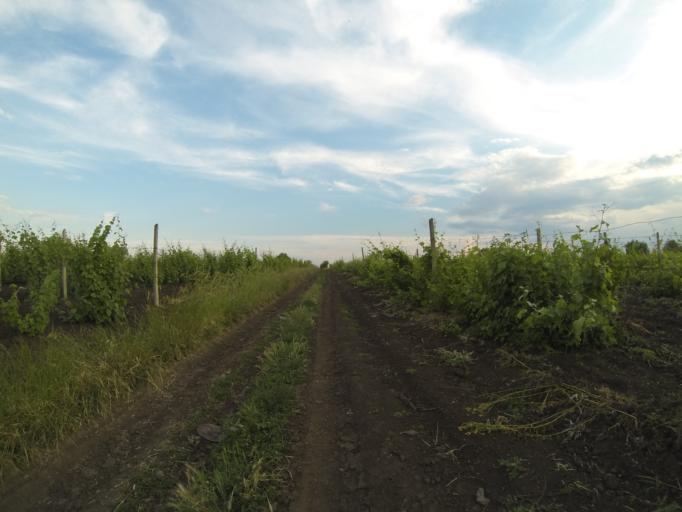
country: RO
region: Dolj
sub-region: Comuna Ceratu
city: Ceratu
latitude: 44.1132
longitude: 23.6824
